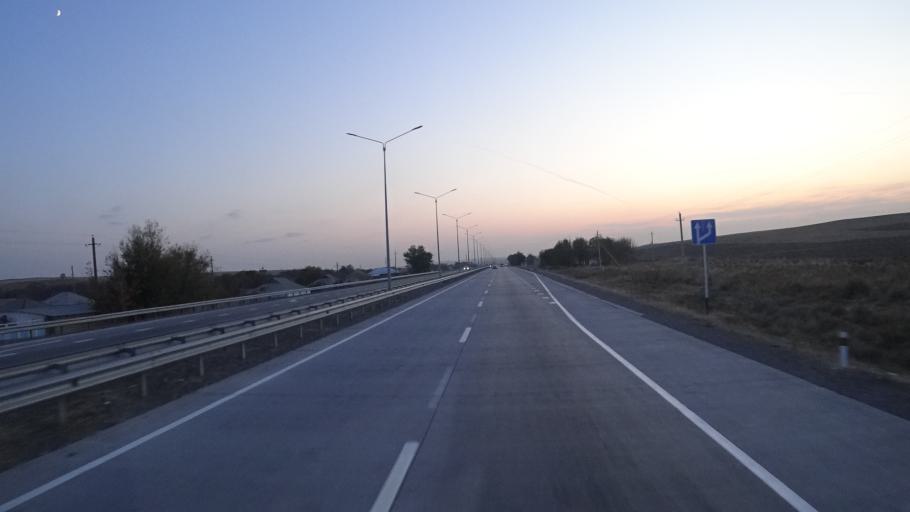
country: KZ
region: Ongtustik Qazaqstan
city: Qazyqurt
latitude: 41.8866
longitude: 69.4430
